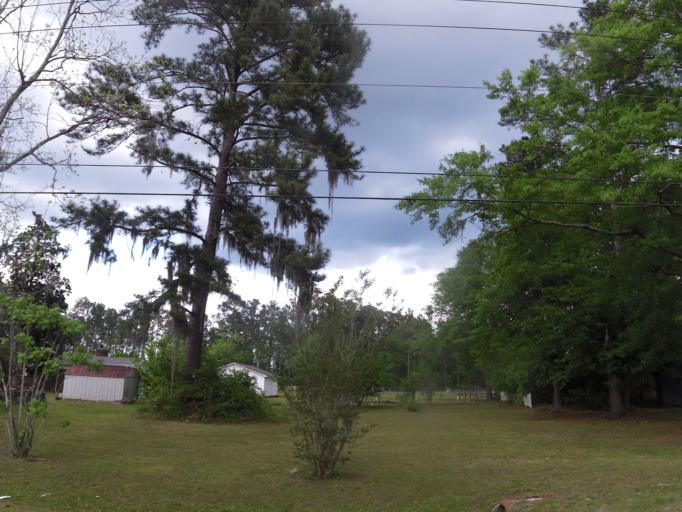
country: US
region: Georgia
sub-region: Charlton County
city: Folkston
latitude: 30.8409
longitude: -81.9956
